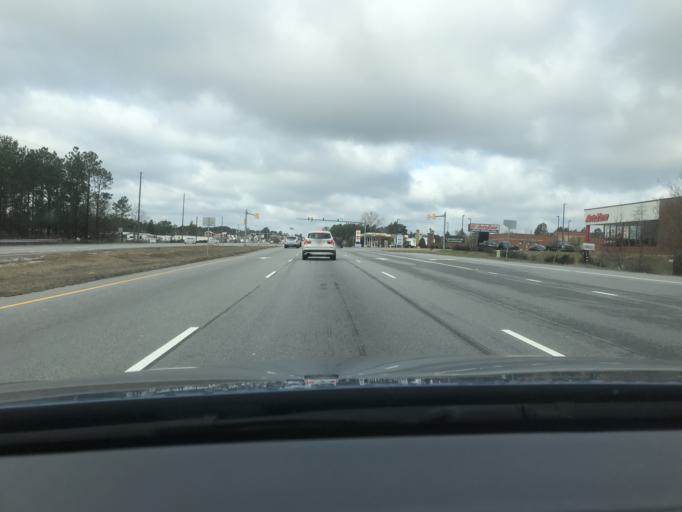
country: US
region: North Carolina
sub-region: Cumberland County
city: Spring Lake
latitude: 35.2529
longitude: -79.0291
